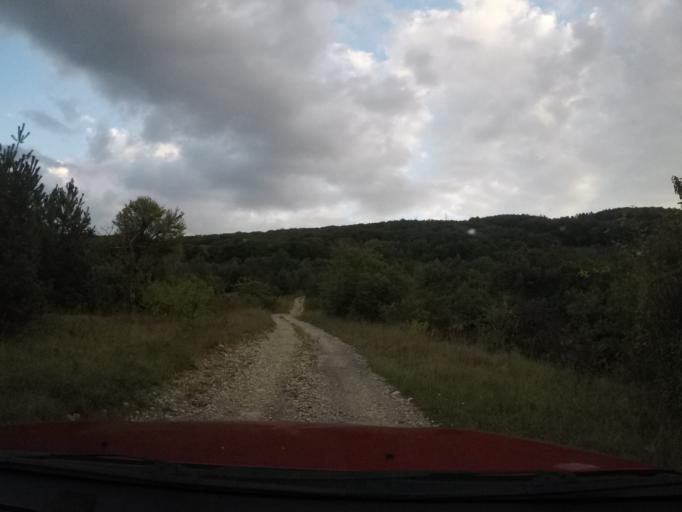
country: SK
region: Kosicky
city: Roznava
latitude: 48.6237
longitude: 20.6228
